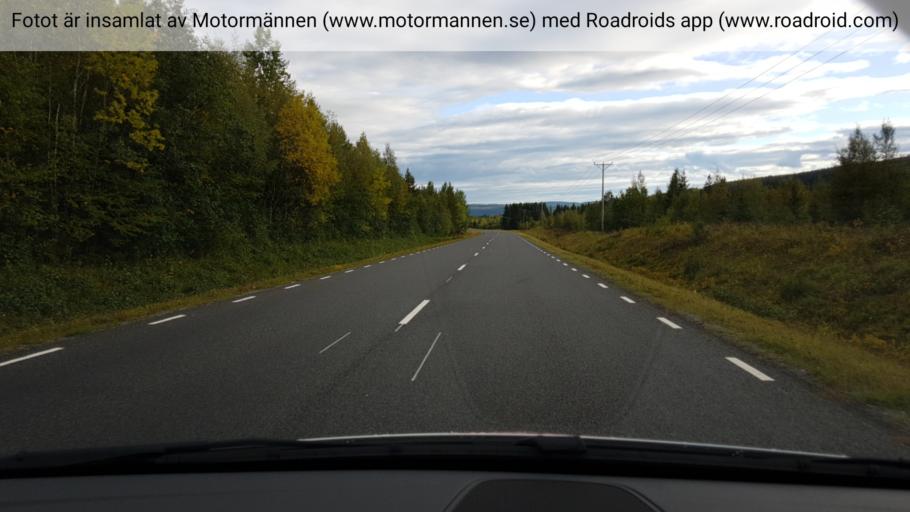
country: SE
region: Jaemtland
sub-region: Are Kommun
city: Jarpen
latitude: 63.3748
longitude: 13.4299
